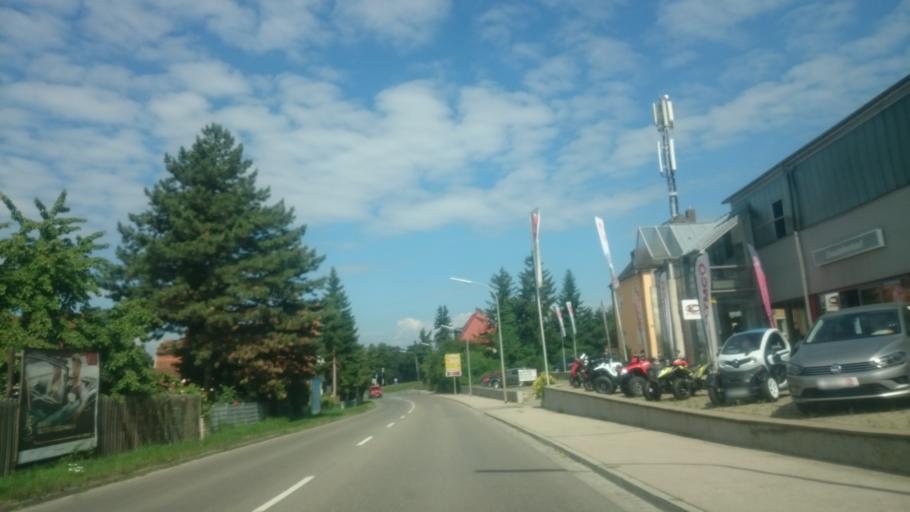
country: DE
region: Bavaria
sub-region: Regierungsbezirk Mittelfranken
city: Weissenburg in Bayern
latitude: 49.0253
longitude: 10.9874
